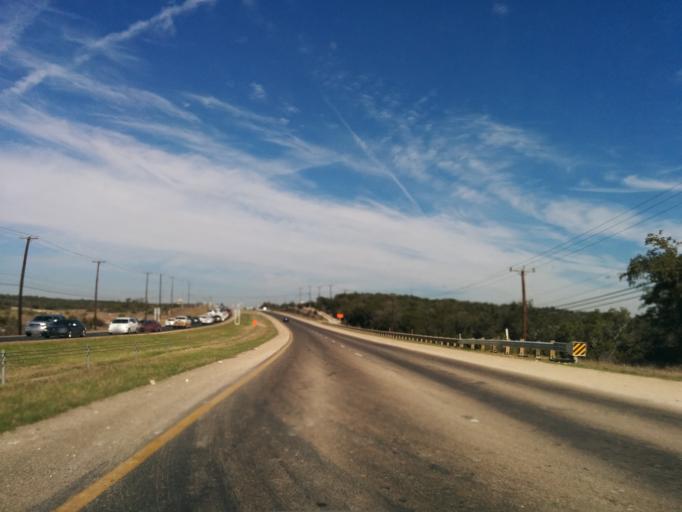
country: US
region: Texas
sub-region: Bexar County
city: Timberwood Park
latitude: 29.6687
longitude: -98.4500
